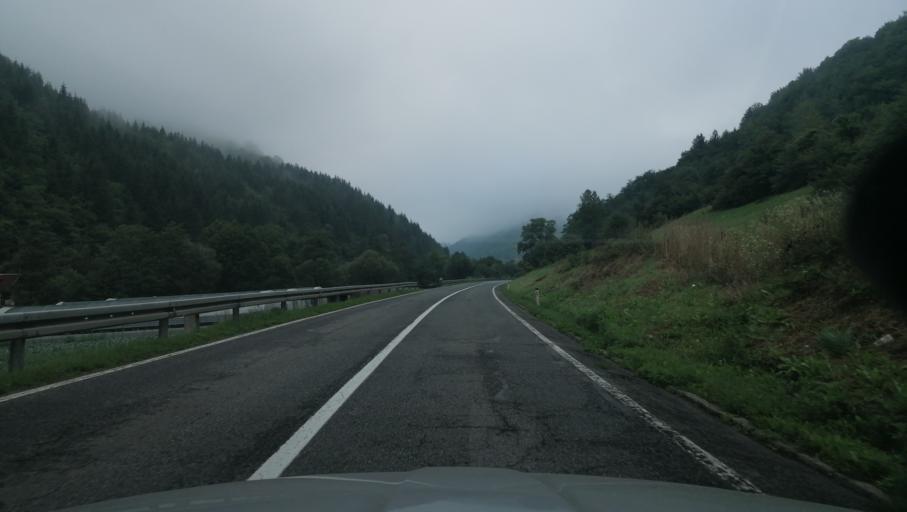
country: BA
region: Federation of Bosnia and Herzegovina
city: Donji Vakuf
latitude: 44.1650
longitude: 17.3609
